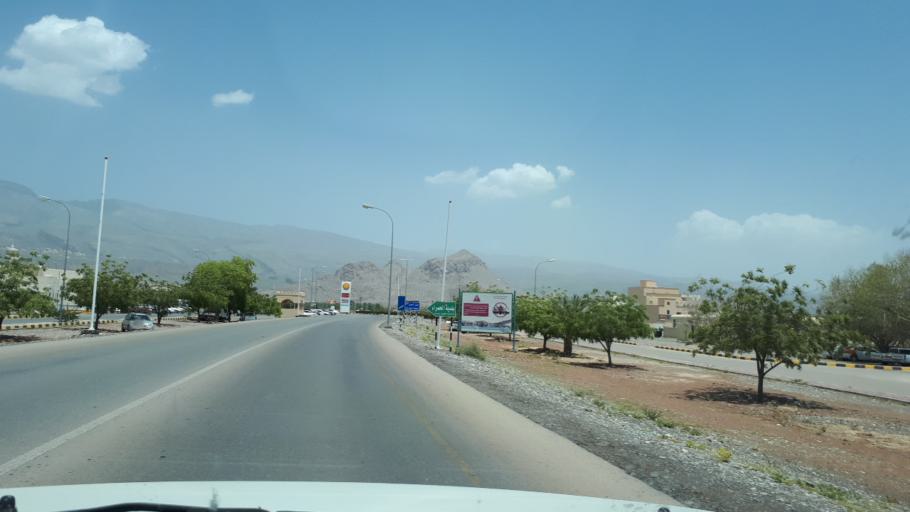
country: OM
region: Muhafazat ad Dakhiliyah
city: Bahla'
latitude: 23.1000
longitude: 57.2758
